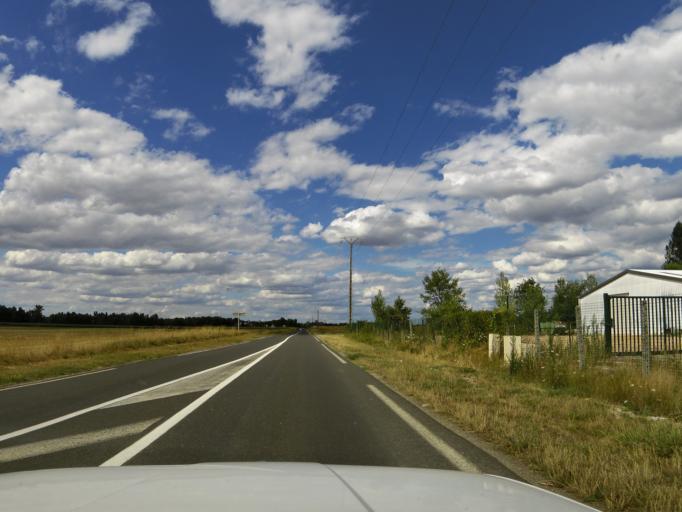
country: FR
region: Rhone-Alpes
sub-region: Departement de l'Ain
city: Loyettes
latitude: 45.7965
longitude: 5.2111
